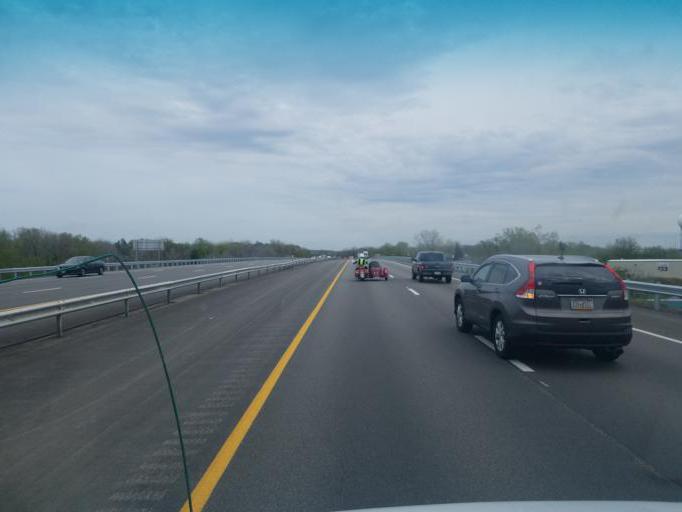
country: US
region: New York
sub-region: Erie County
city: Williamsville
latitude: 42.9517
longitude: -78.7412
